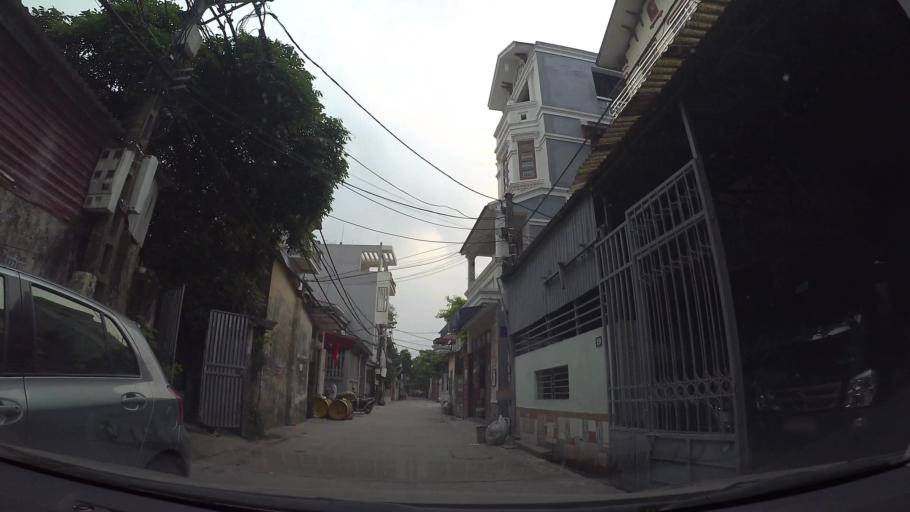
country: VN
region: Ha Noi
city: Hoan Kiem
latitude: 21.0720
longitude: 105.8884
